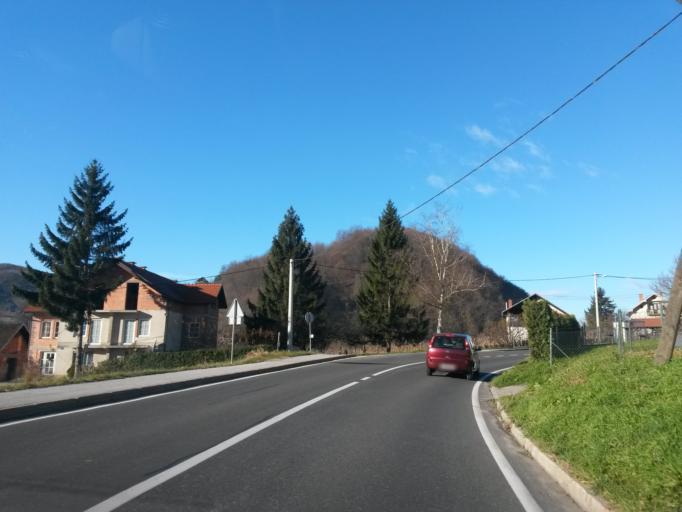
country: HR
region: Varazdinska
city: Lepoglava
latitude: 46.2077
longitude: 16.0218
